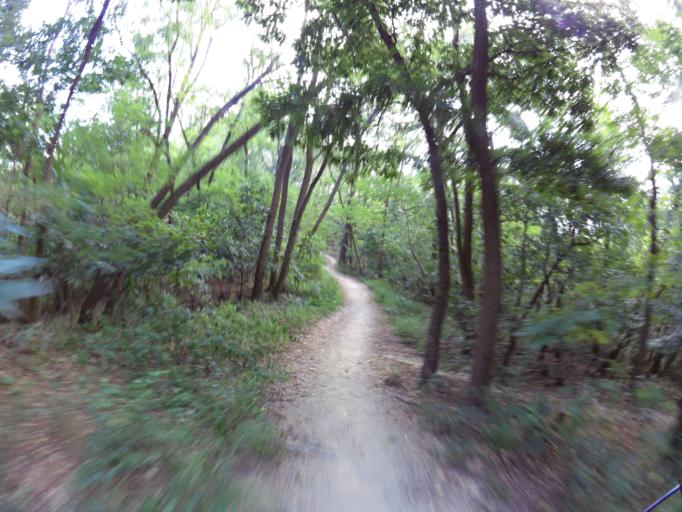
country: KR
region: Daegu
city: Daegu
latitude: 35.8594
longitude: 128.6520
